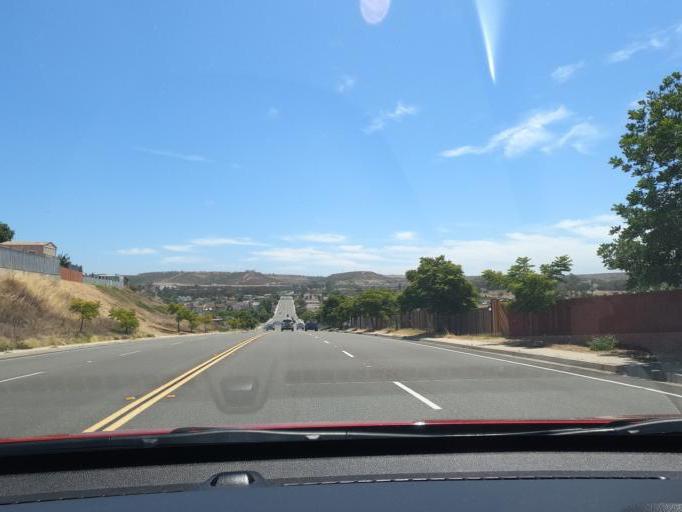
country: US
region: California
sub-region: San Diego County
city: Imperial Beach
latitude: 32.5736
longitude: -117.0480
